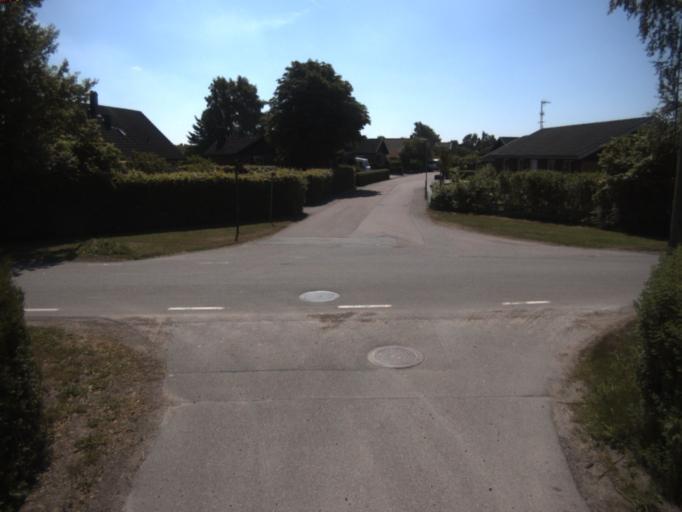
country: SE
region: Skane
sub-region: Helsingborg
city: Odakra
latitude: 56.1261
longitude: 12.6965
